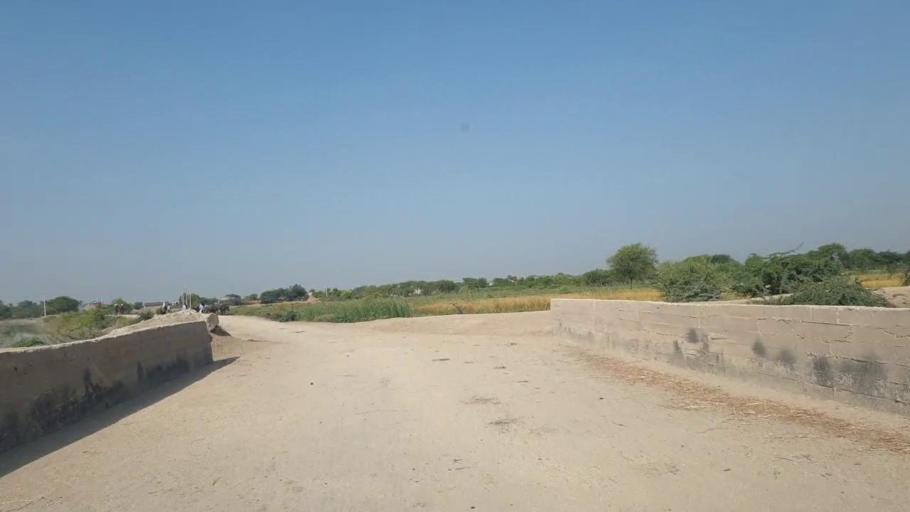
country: PK
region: Sindh
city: Badin
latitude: 24.5218
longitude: 68.7659
